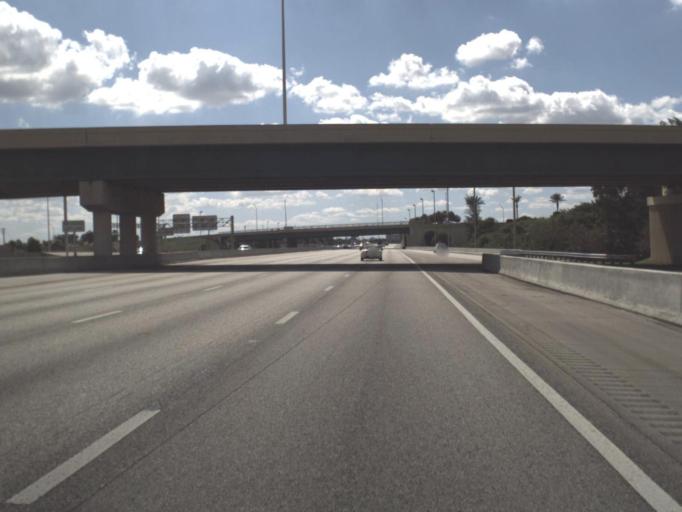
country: US
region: Florida
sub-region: Broward County
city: Palm Aire
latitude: 26.1946
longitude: -80.2088
